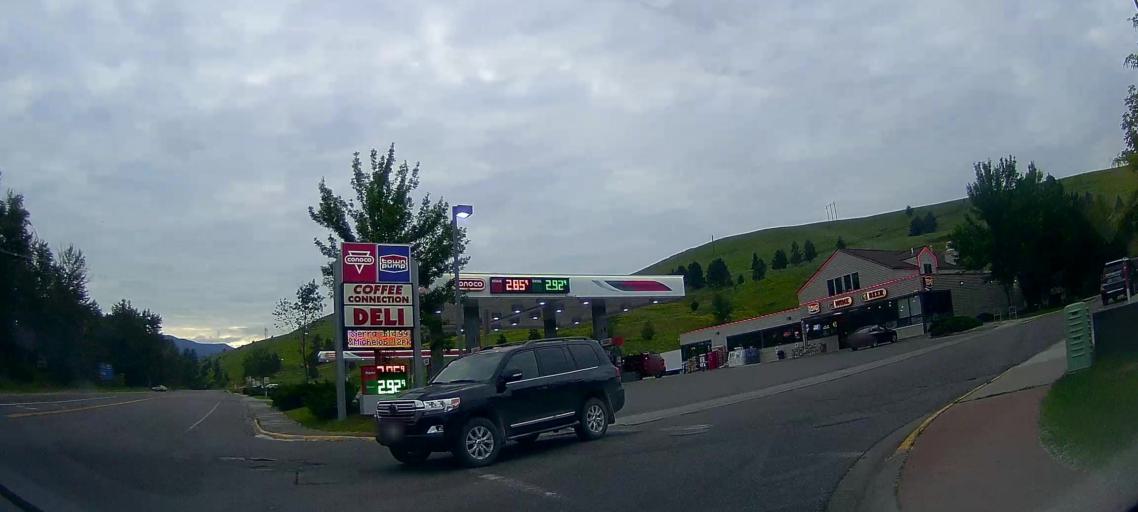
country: US
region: Montana
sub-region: Missoula County
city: Orchard Homes
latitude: 46.9146
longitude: -114.0332
